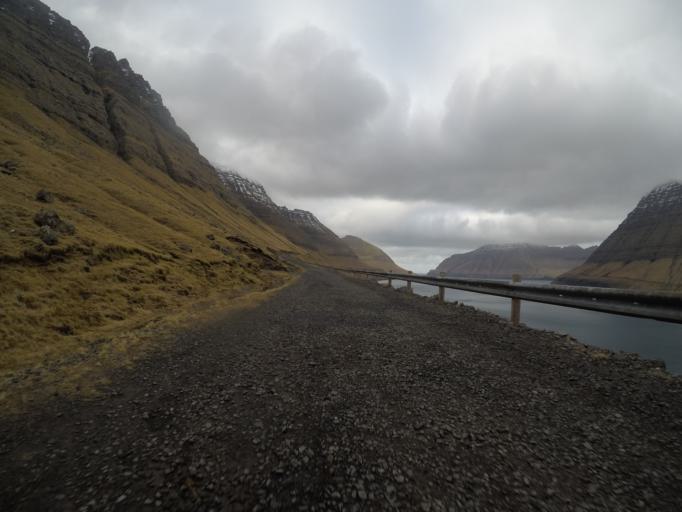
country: FO
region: Nordoyar
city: Klaksvik
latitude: 62.3241
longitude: -6.5626
